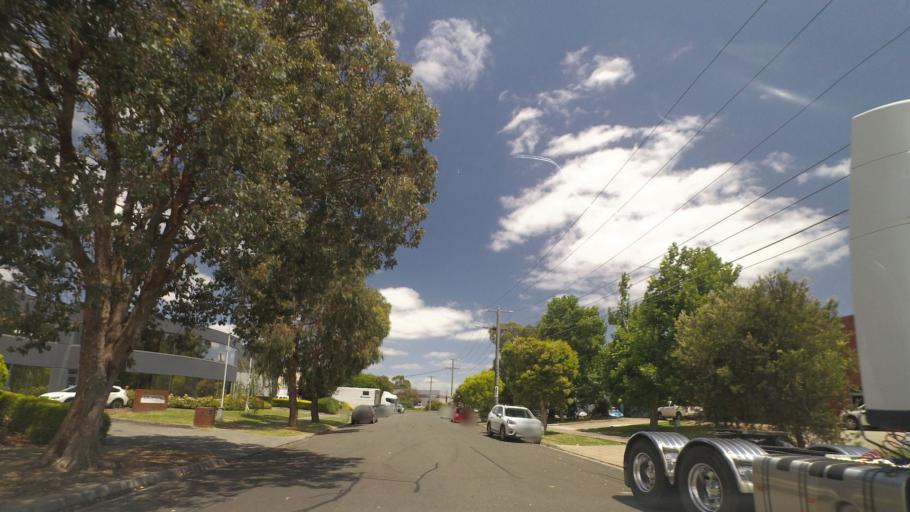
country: AU
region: Victoria
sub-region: Maroondah
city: Bayswater North
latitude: -37.8225
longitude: 145.2852
